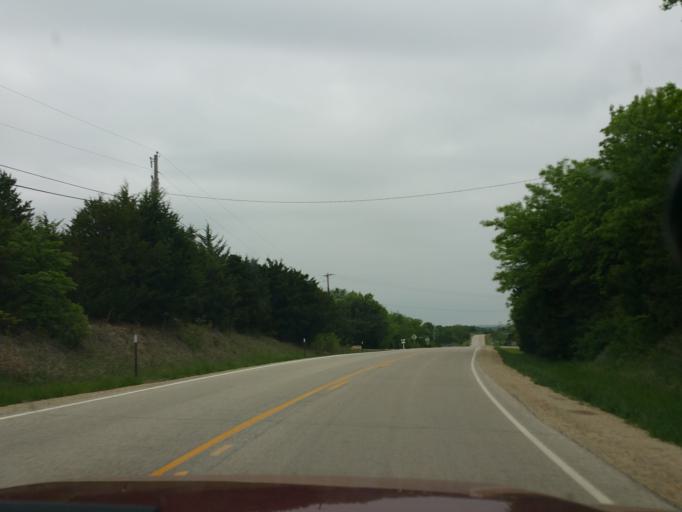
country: US
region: Kansas
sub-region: Riley County
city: Manhattan
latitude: 39.2665
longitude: -96.6220
